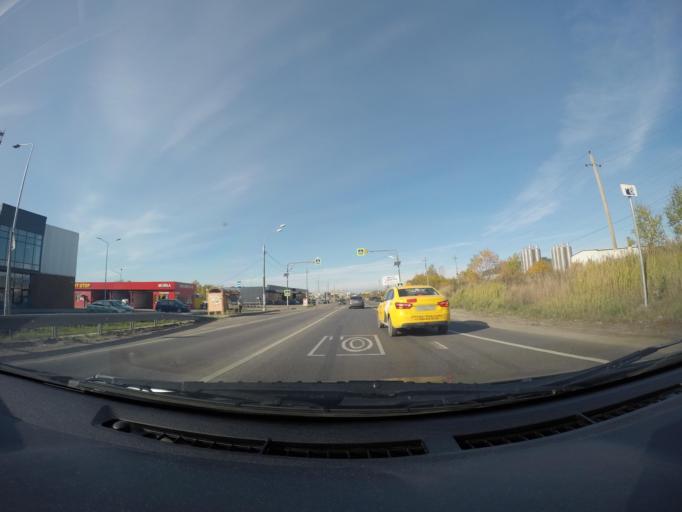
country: RU
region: Moskovskaya
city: Rechitsy
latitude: 55.6037
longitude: 38.4347
